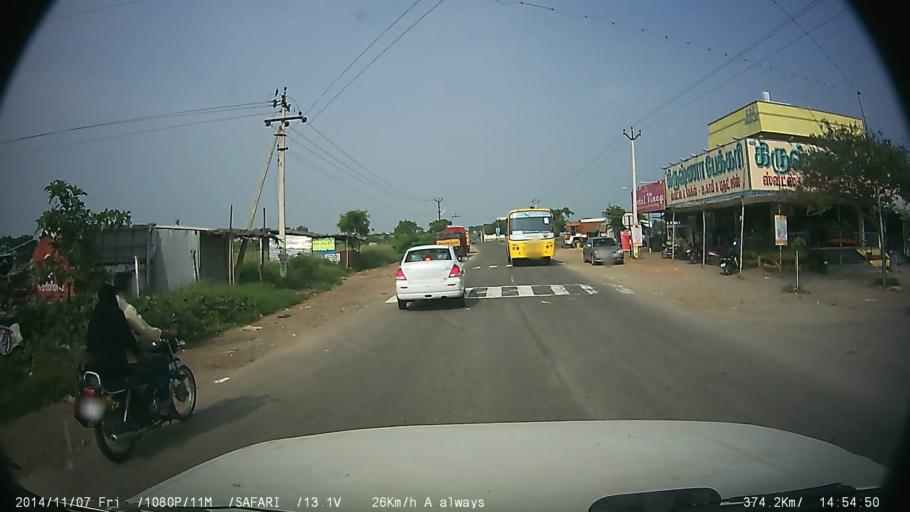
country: IN
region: Tamil Nadu
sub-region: Tiruppur
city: Uttukkuli
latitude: 11.1585
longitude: 77.4275
